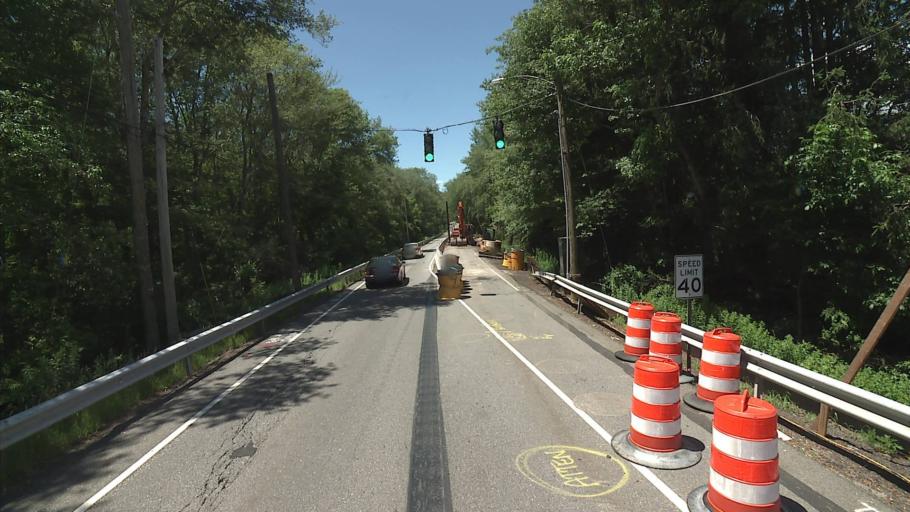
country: US
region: Connecticut
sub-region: New London County
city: Pawcatuck
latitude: 41.3822
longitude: -71.8737
